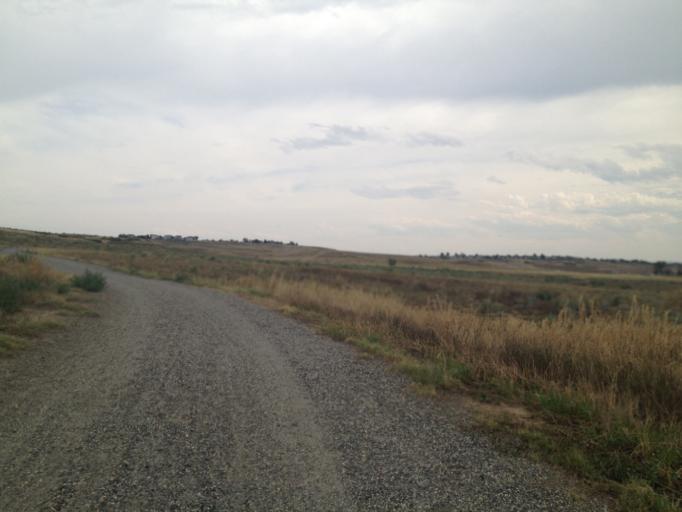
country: US
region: Colorado
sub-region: Broomfield County
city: Broomfield
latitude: 39.9561
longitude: -105.0860
